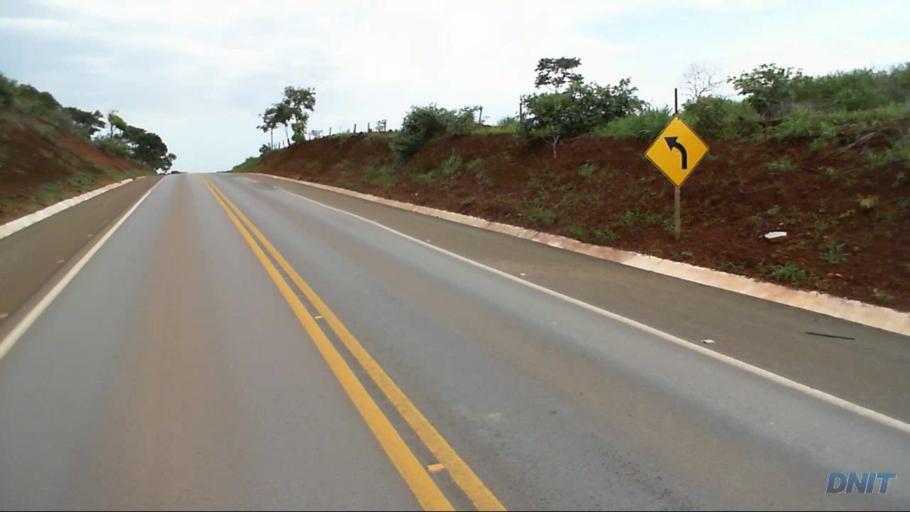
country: BR
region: Goias
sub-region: Barro Alto
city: Barro Alto
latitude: -14.8876
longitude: -48.9790
